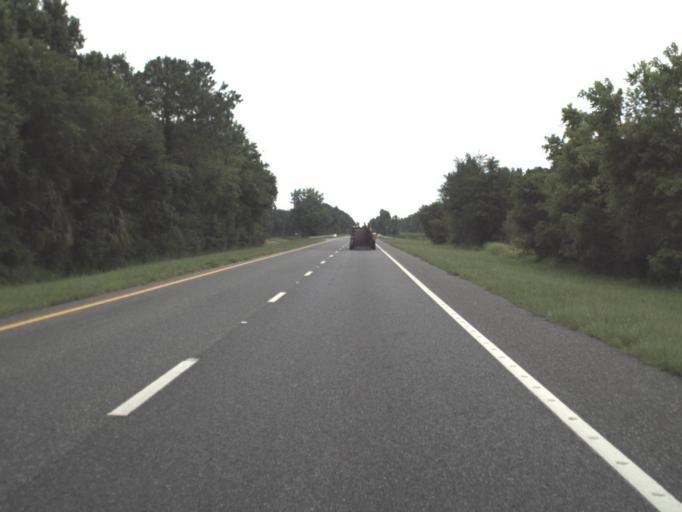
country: US
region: Florida
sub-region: Levy County
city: Bronson
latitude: 29.2898
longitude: -82.7454
